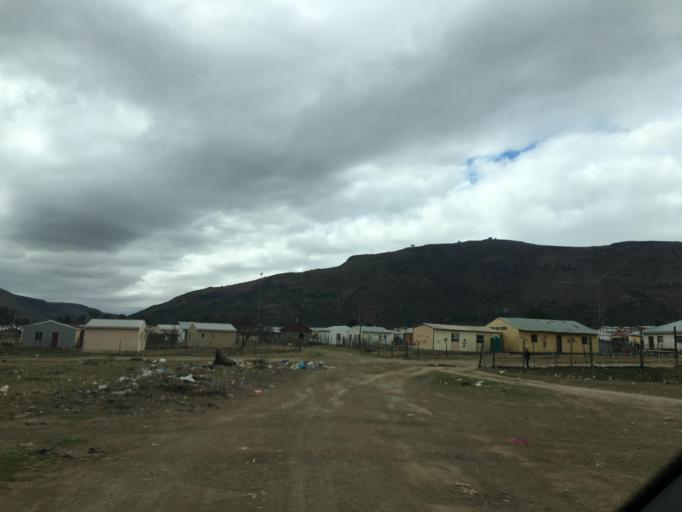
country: ZA
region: Eastern Cape
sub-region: Chris Hani District Municipality
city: Cala
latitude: -31.5362
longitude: 27.6995
